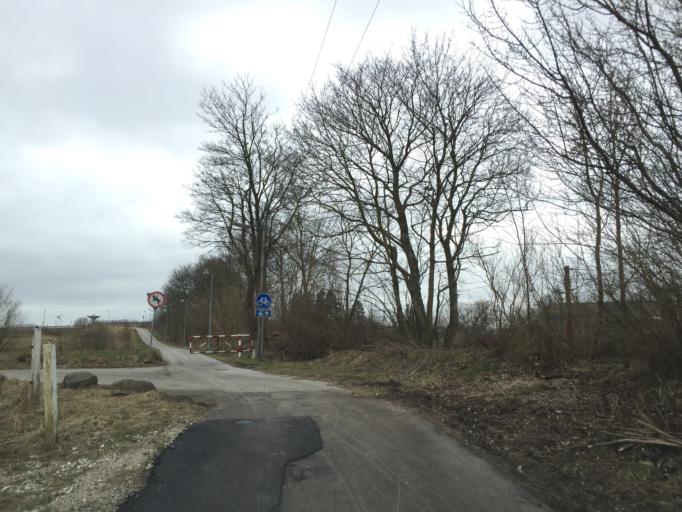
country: DK
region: Capital Region
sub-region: Allerod Kommune
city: Lillerod
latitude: 55.9000
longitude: 12.3312
